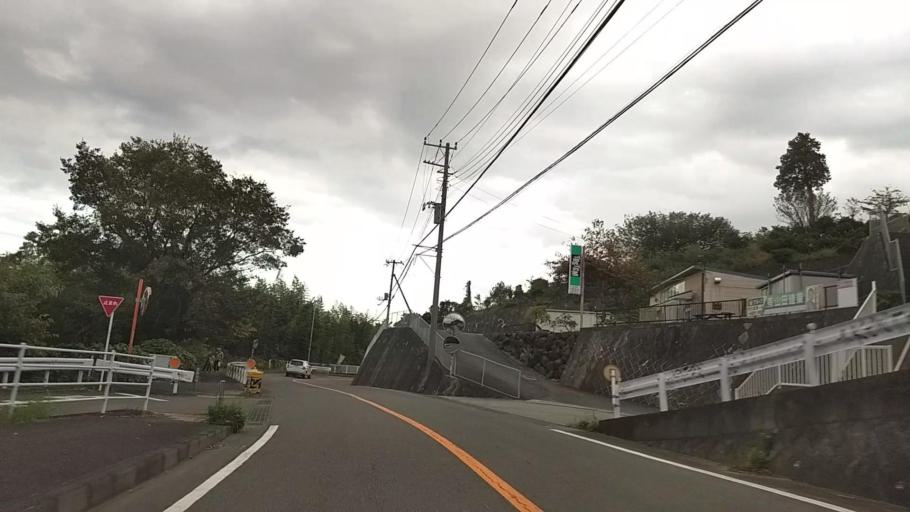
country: JP
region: Kanagawa
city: Yugawara
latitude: 35.1680
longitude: 139.1355
